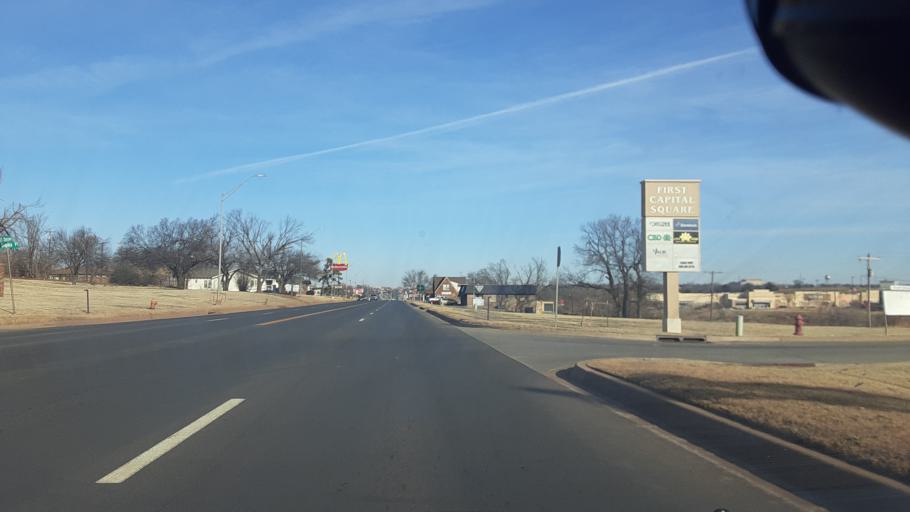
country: US
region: Oklahoma
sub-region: Logan County
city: Guthrie
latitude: 35.8586
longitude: -97.4254
